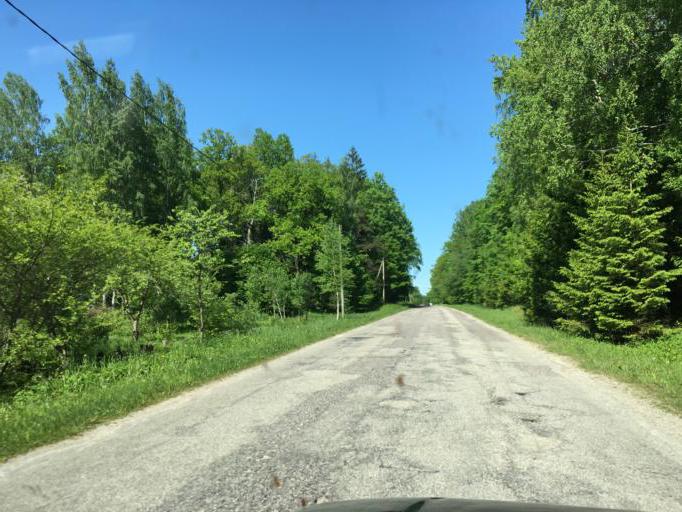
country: LV
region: Dundaga
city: Dundaga
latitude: 57.4957
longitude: 22.3461
